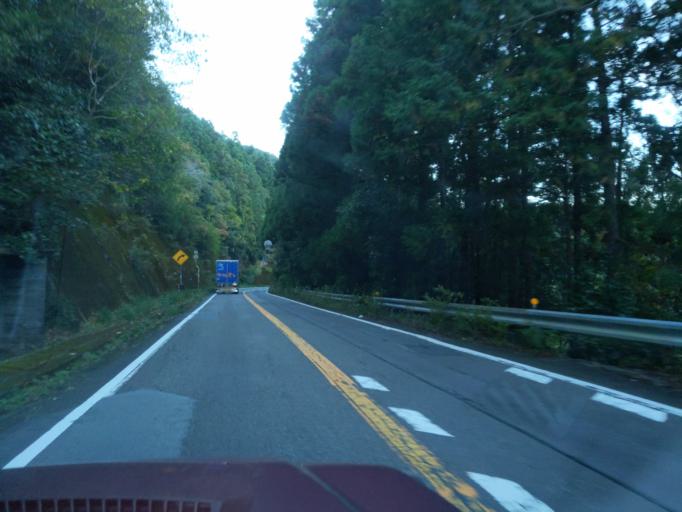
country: JP
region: Tokushima
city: Anan
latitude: 33.7034
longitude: 134.4445
